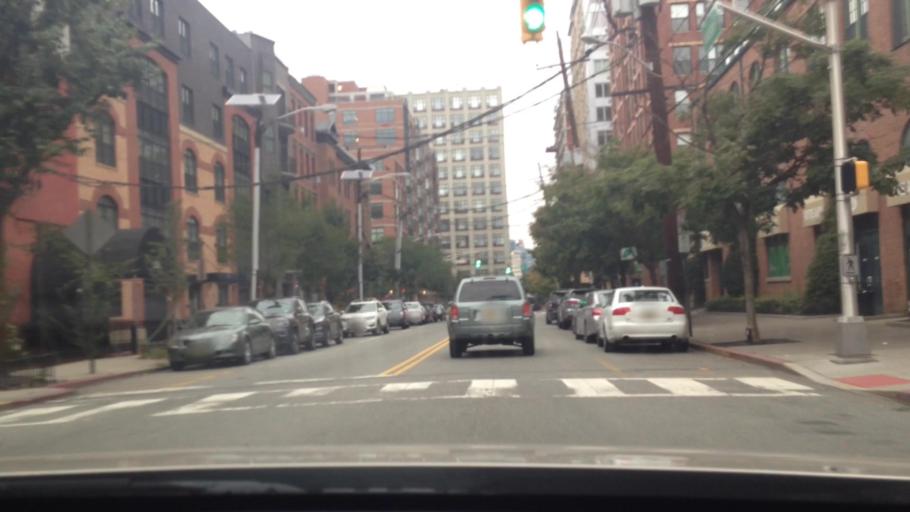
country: US
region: New Jersey
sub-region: Hudson County
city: Hoboken
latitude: 40.7521
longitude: -74.0253
